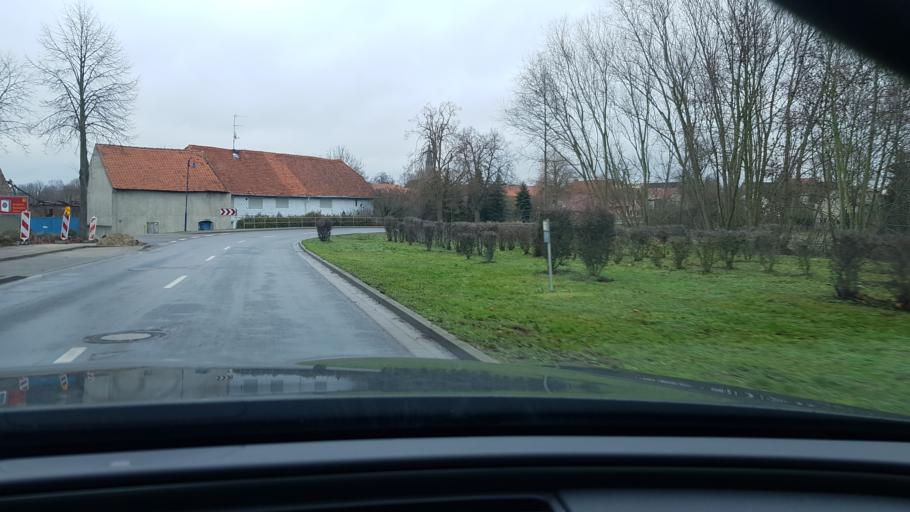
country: DE
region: Saxony-Anhalt
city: Weferlingen
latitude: 52.4037
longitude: 11.1084
